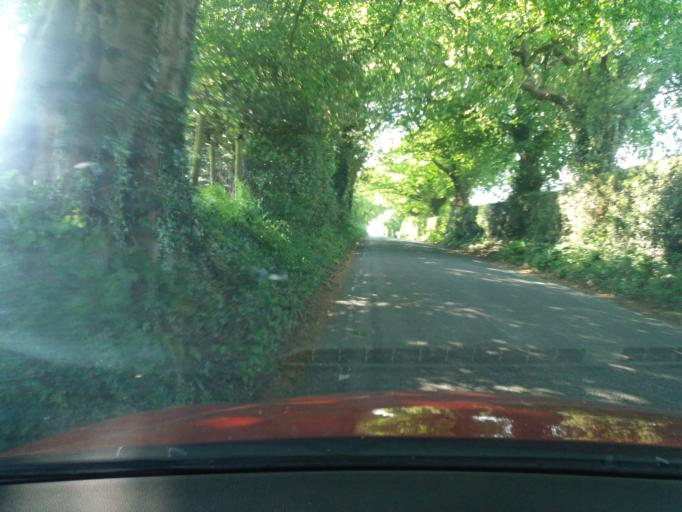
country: GB
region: England
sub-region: Lancashire
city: Chorley
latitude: 53.6737
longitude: -2.5891
